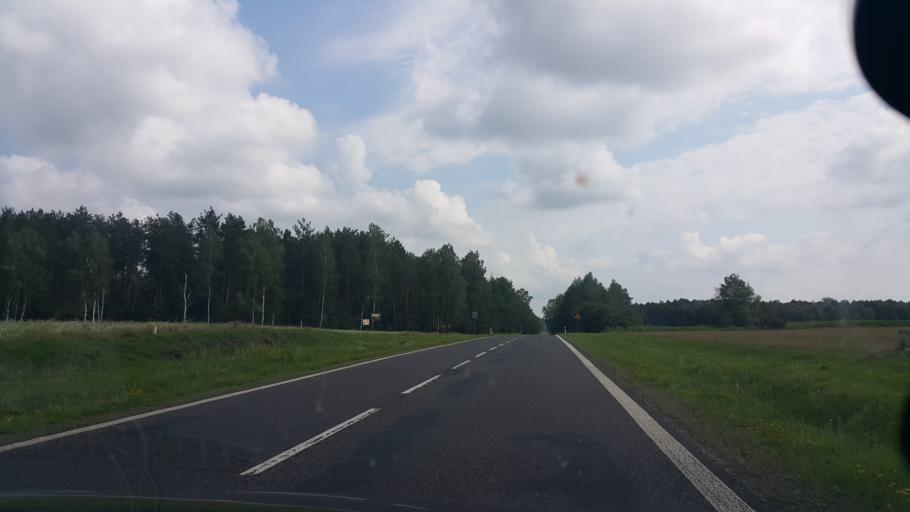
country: PL
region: Lublin Voivodeship
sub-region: Powiat wlodawski
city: Hansk
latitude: 51.4810
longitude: 23.3394
